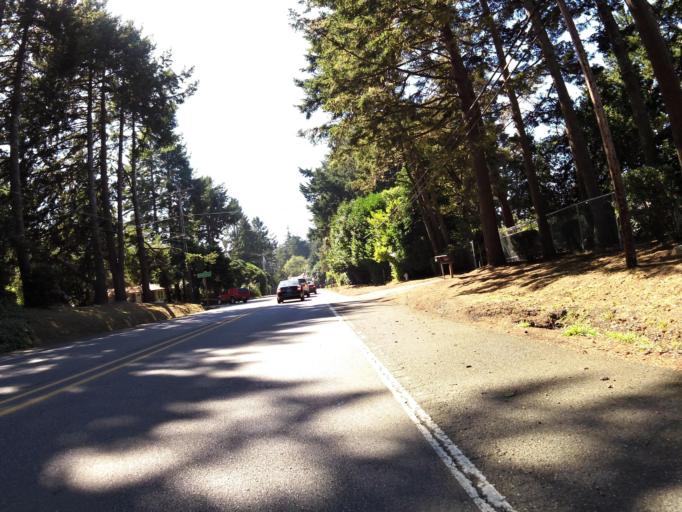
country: US
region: Oregon
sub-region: Coos County
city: Barview
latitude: 43.3486
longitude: -124.3143
